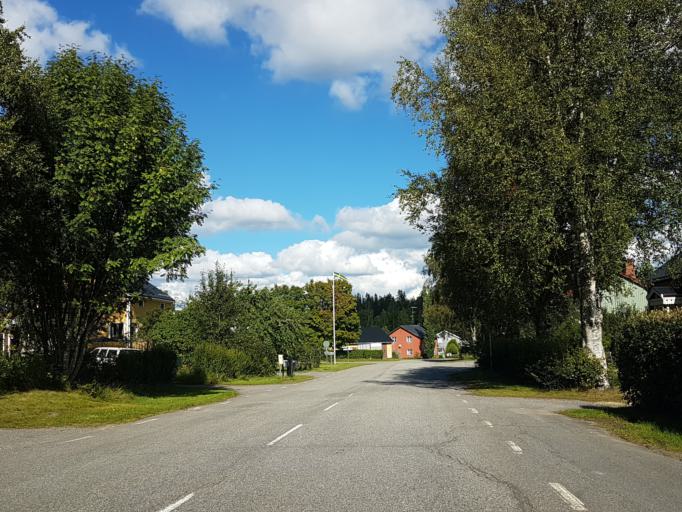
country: SE
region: Vaesterbotten
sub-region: Skelleftea Kommun
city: Burtraesk
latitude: 64.2676
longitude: 20.4925
